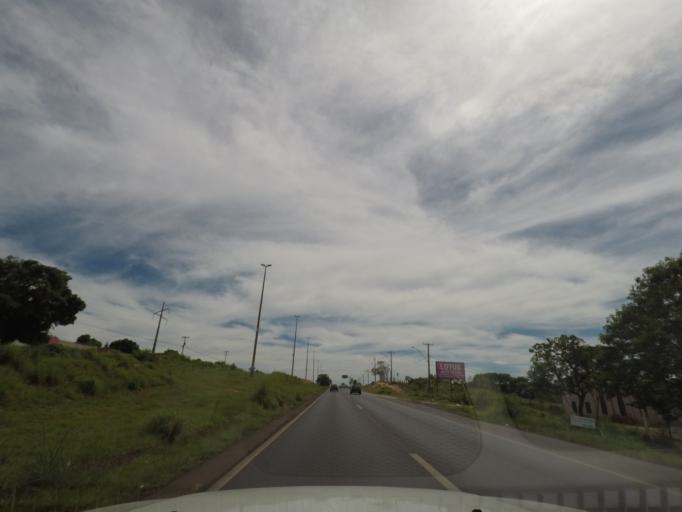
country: BR
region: Goias
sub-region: Planaltina
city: Planaltina
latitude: -15.6031
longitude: -47.6843
